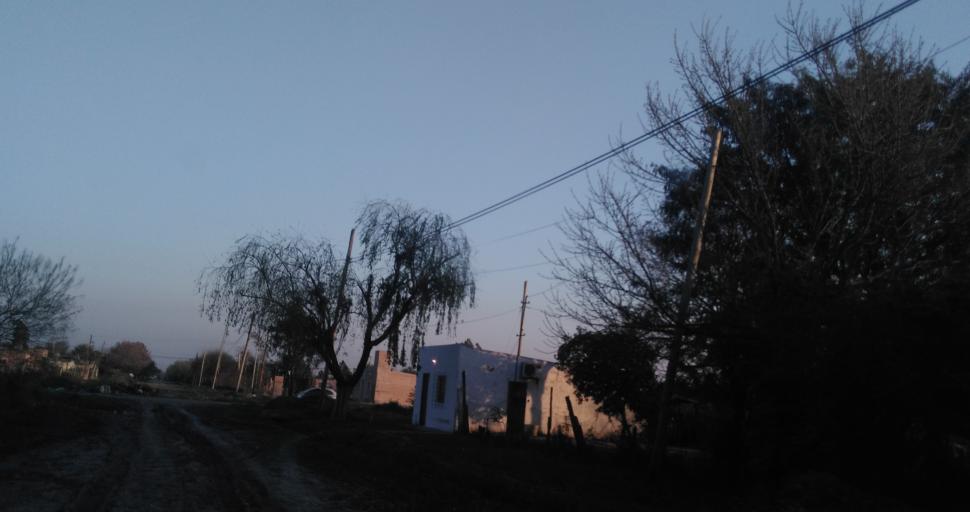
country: AR
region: Chaco
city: Resistencia
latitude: -27.4818
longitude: -59.0023
